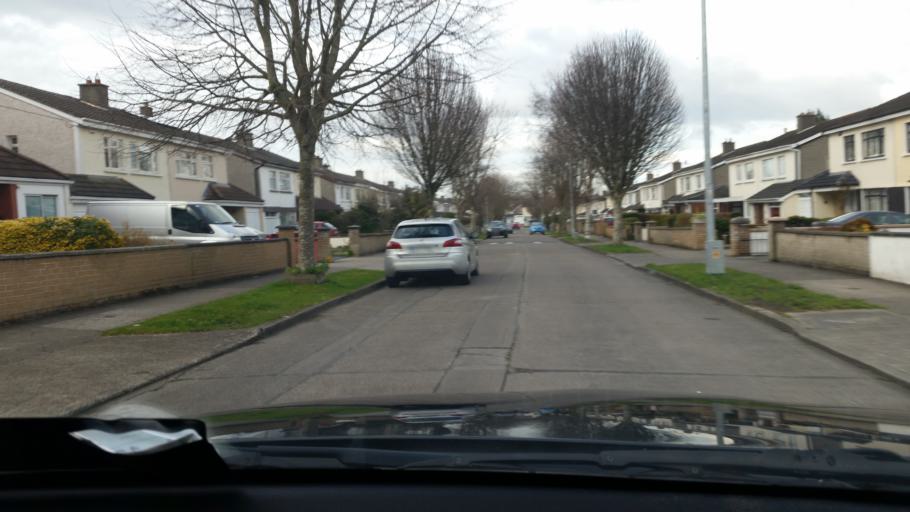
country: IE
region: Leinster
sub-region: Fingal County
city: Blanchardstown
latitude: 53.3845
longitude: -6.3866
